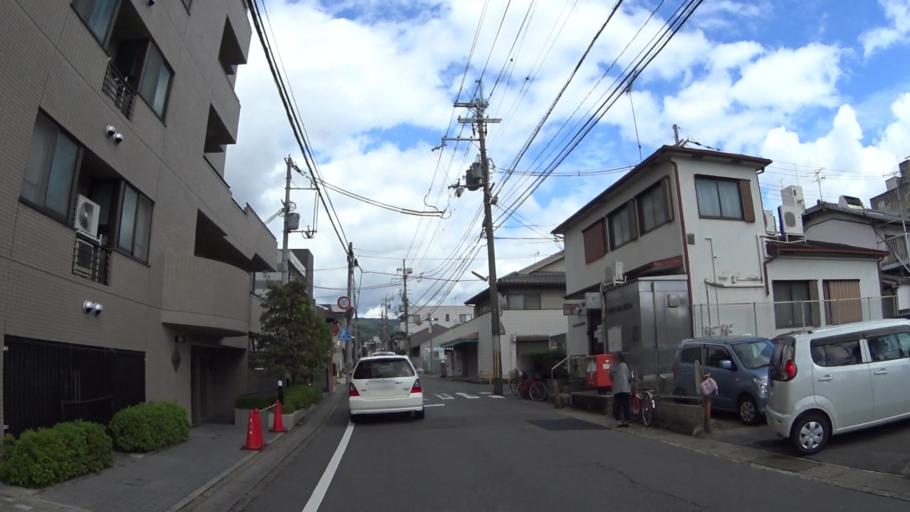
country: JP
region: Shiga Prefecture
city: Otsu-shi
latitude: 34.9767
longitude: 135.8148
